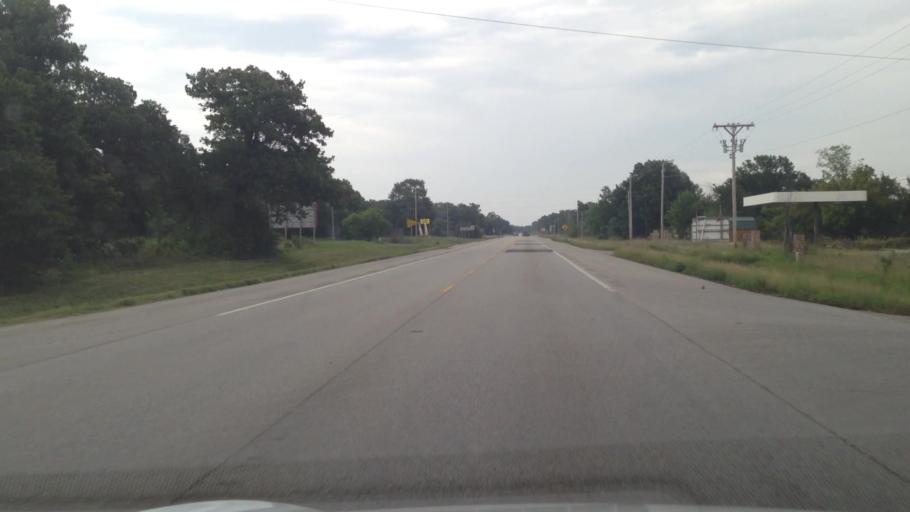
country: US
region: Kansas
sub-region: Cherokee County
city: Galena
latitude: 37.0236
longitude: -94.6492
